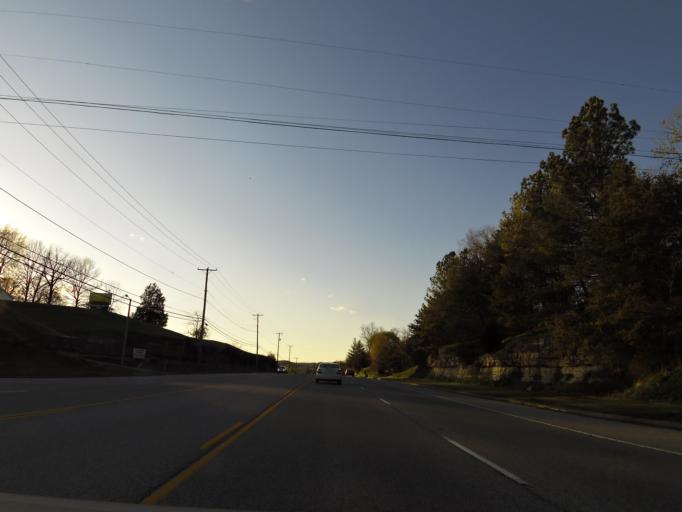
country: US
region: Tennessee
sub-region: Sumner County
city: Millersville
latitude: 36.3627
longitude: -86.7302
